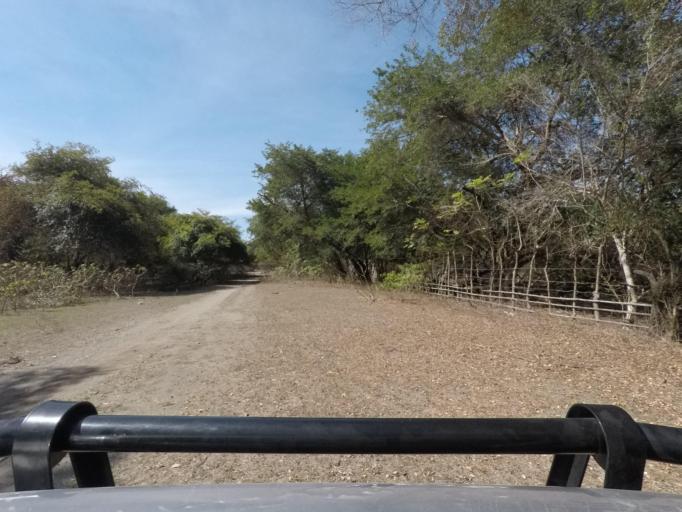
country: TL
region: Bobonaro
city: Maliana
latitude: -8.8780
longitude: 125.0088
